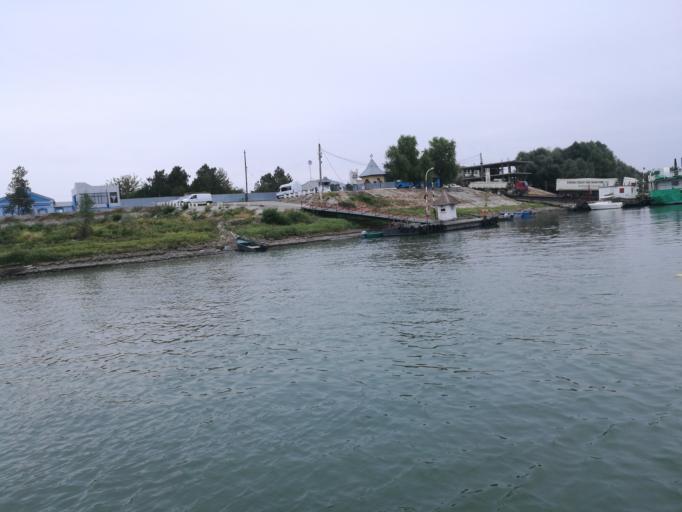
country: RO
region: Braila
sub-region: Municipiul Braila
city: Braila
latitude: 45.2860
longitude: 27.9965
